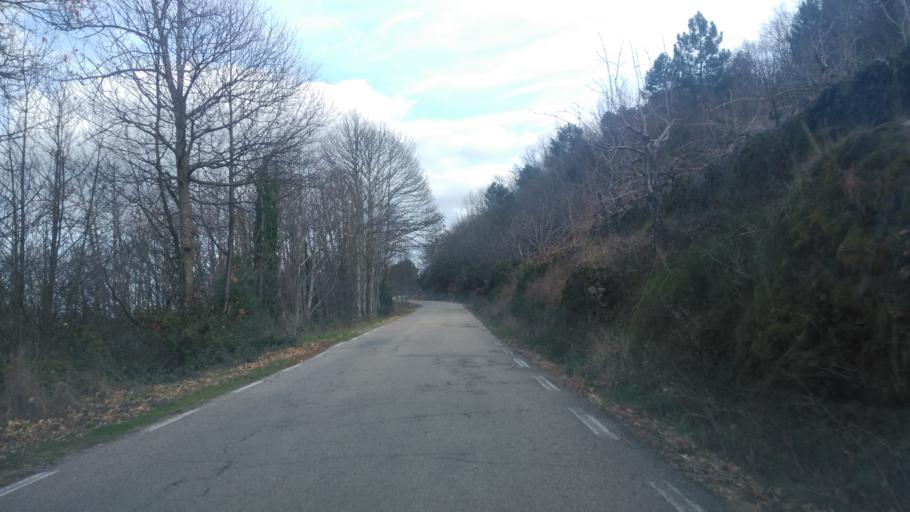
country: ES
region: Castille and Leon
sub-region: Provincia de Salamanca
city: Mogarraz
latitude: 40.4948
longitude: -6.0469
